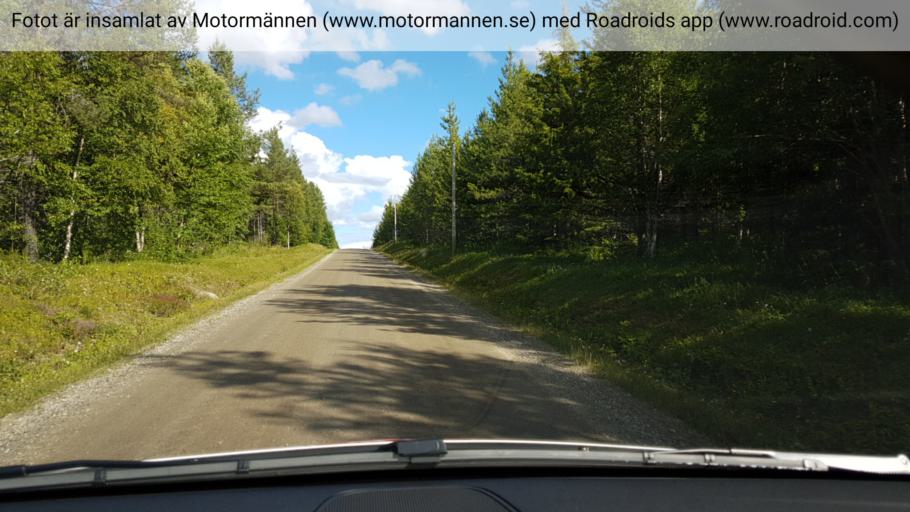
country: SE
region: Jaemtland
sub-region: Ragunda Kommun
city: Hammarstrand
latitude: 63.2800
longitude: 15.9459
